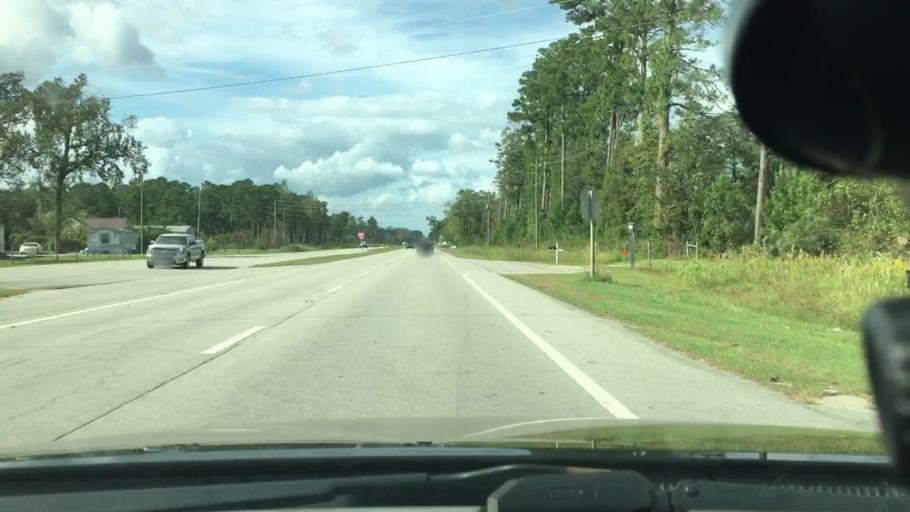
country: US
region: North Carolina
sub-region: Craven County
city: New Bern
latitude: 35.1461
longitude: -77.0317
